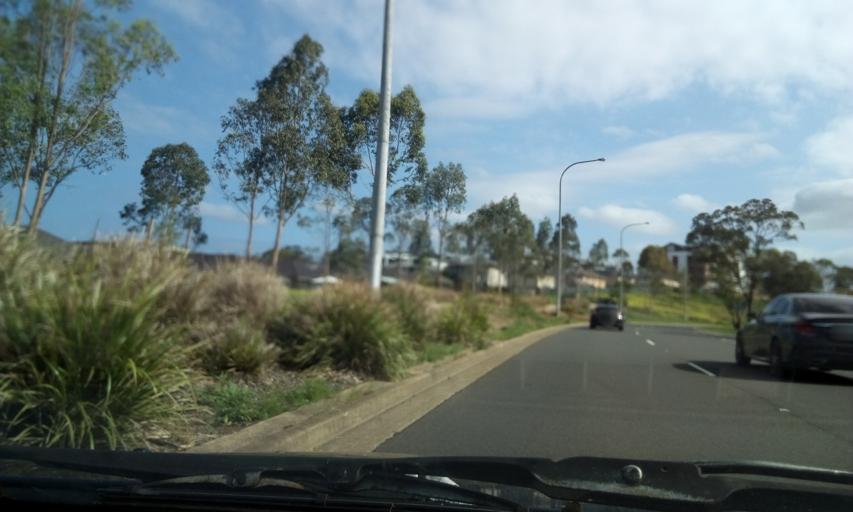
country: AU
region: New South Wales
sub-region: Campbelltown Municipality
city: Glen Alpine
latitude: -34.0767
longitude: 150.7998
